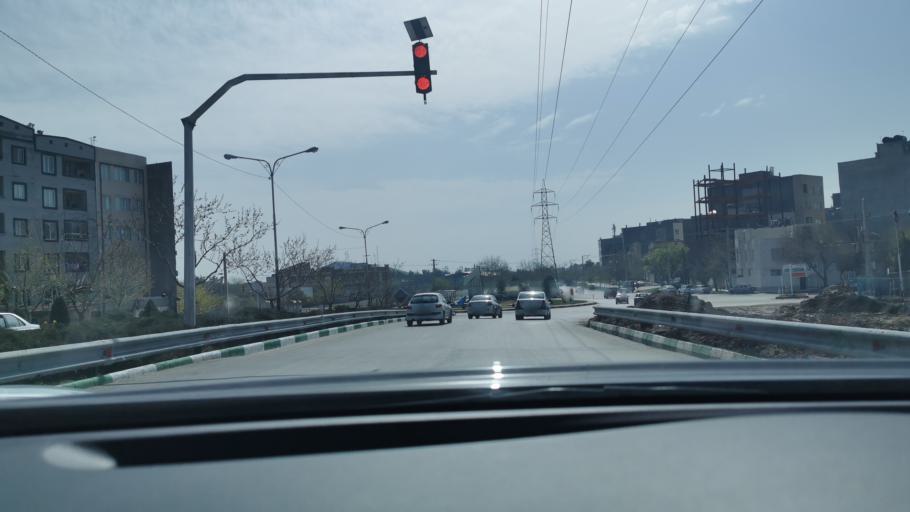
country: IR
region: Razavi Khorasan
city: Mashhad
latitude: 36.2836
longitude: 59.5431
